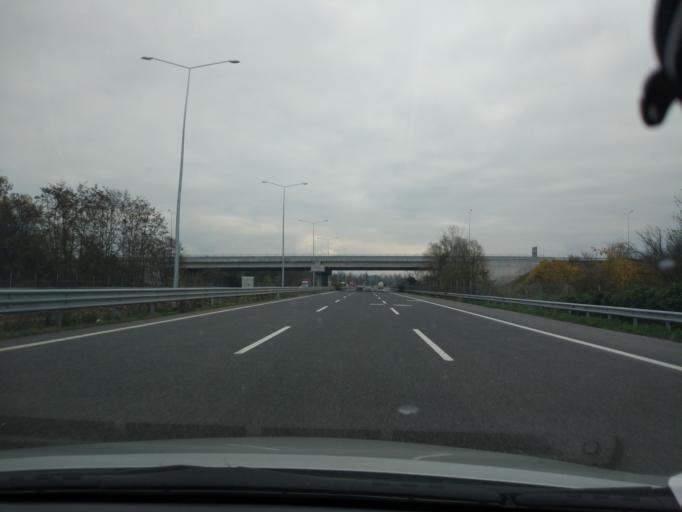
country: TR
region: Duzce
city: Duzce
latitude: 40.8041
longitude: 31.1664
